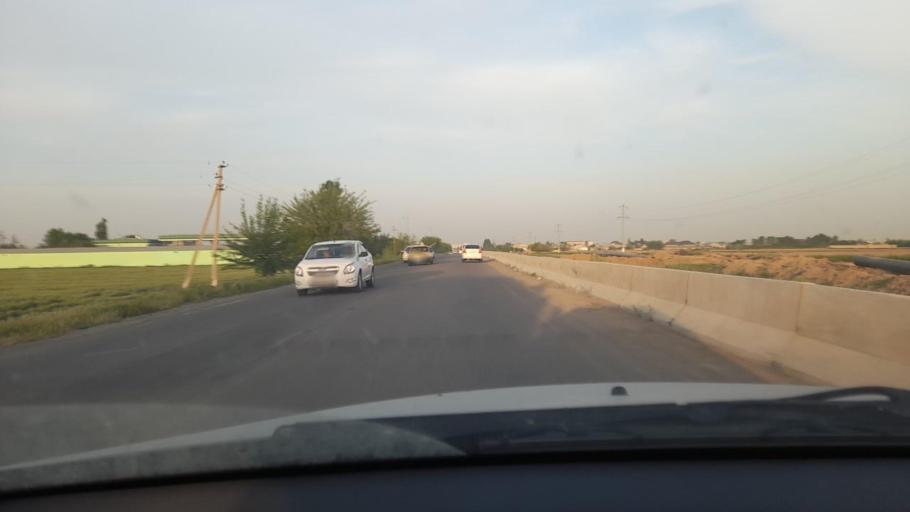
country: UZ
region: Sirdaryo
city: Guliston
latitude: 40.5078
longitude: 68.7378
